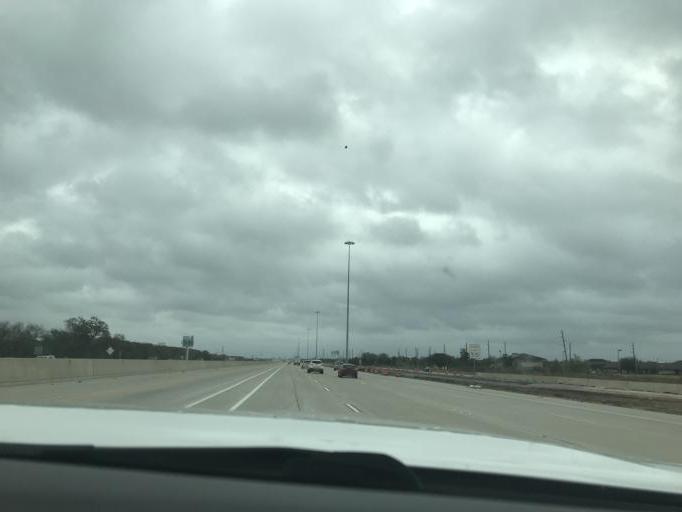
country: US
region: Texas
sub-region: Fort Bend County
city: Greatwood
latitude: 29.5579
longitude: -95.7085
